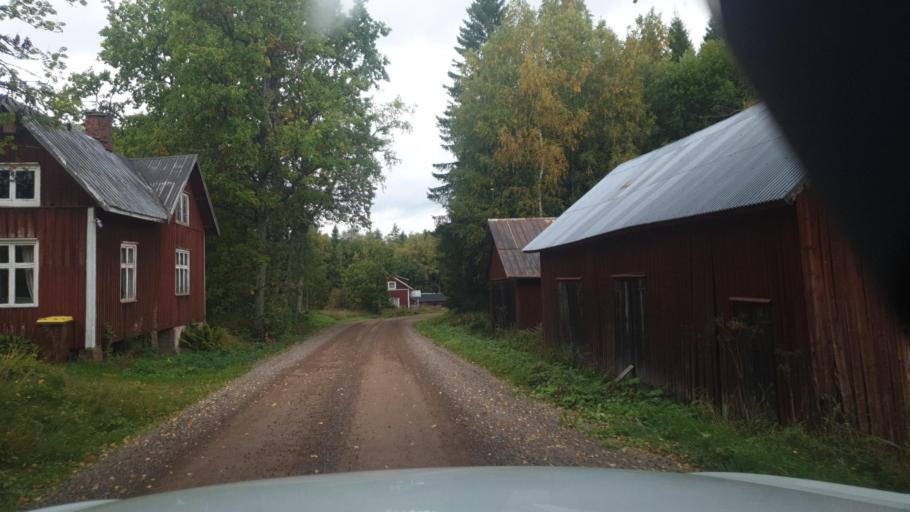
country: SE
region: Vaermland
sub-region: Arvika Kommun
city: Arvika
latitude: 59.9744
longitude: 12.6593
